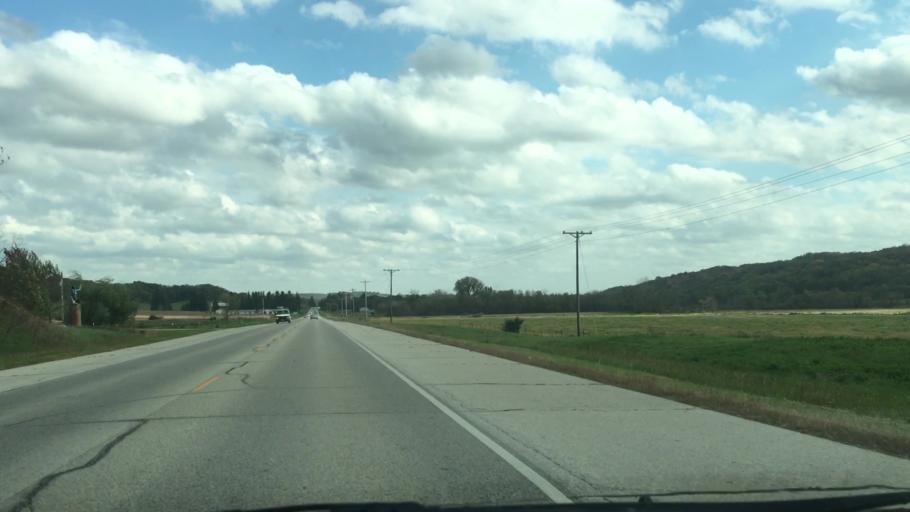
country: US
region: Minnesota
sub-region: Fillmore County
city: Chatfield
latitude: 43.8786
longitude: -92.2179
